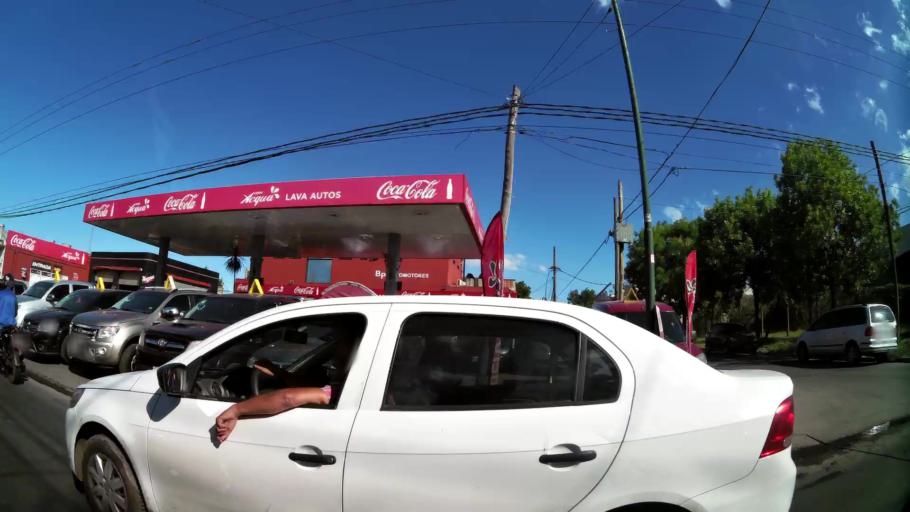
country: AR
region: Buenos Aires
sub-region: Partido de Tigre
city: Tigre
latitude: -34.4676
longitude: -58.5585
